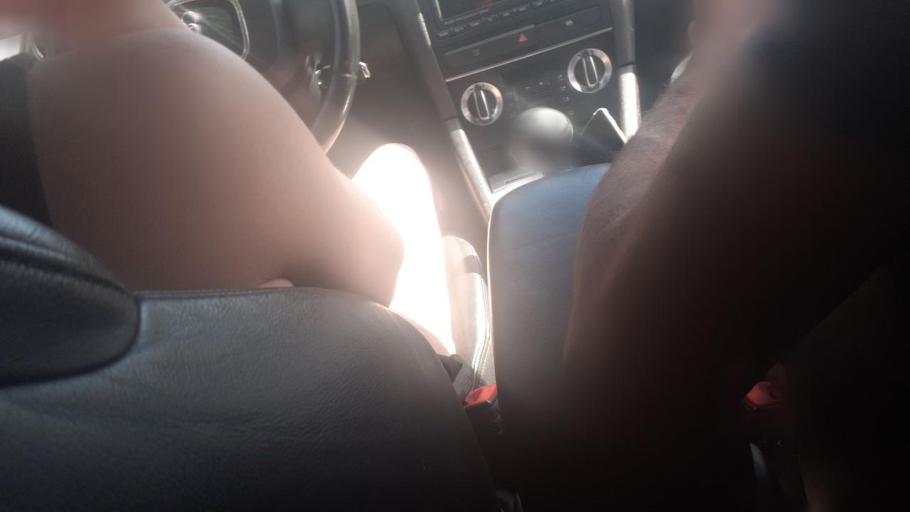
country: FR
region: Haute-Normandie
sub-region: Departement de la Seine-Maritime
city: Grand-Couronne
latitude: 49.3636
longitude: 1.0060
